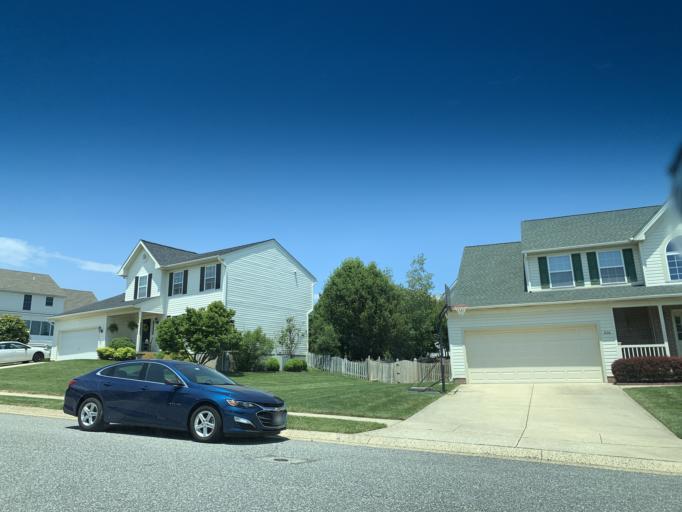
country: US
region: Maryland
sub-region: Harford County
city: Bel Air North
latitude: 39.5648
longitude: -76.3844
